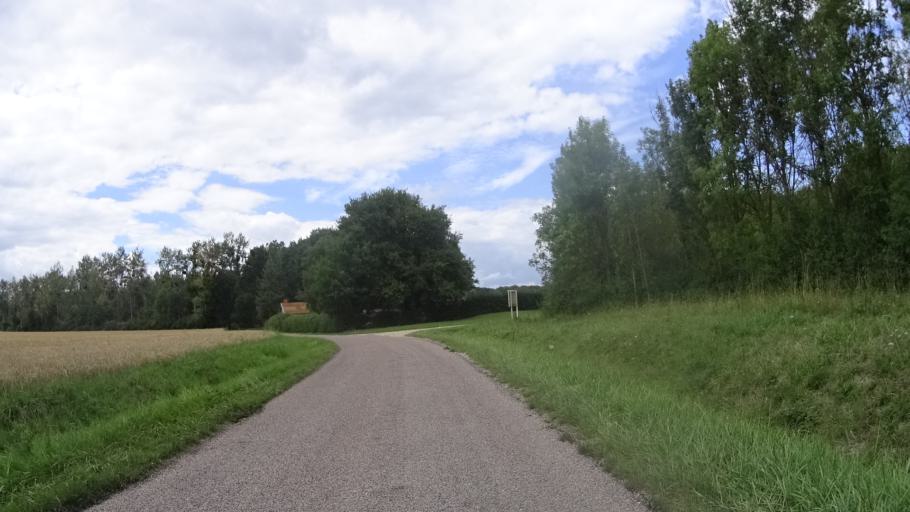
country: FR
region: Champagne-Ardenne
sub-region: Departement de la Haute-Marne
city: Villiers-en-Lieu
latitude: 48.6041
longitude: 4.8600
